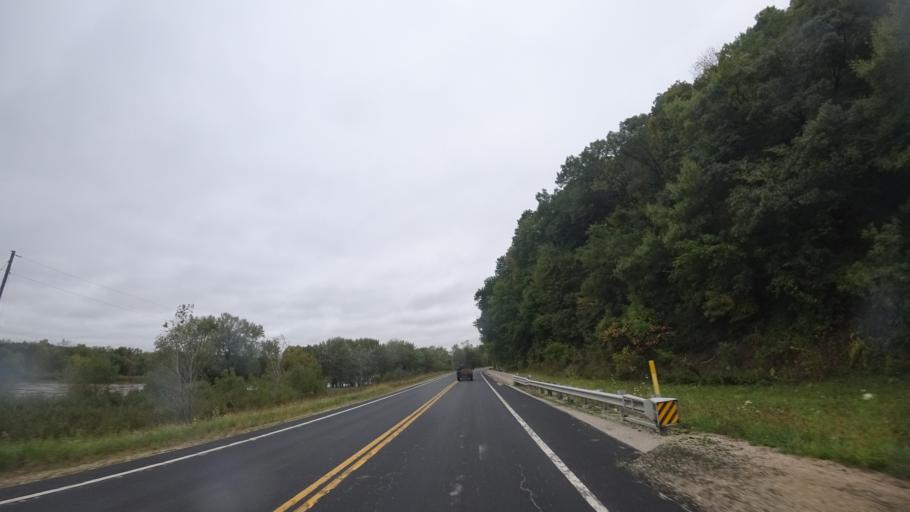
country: US
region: Wisconsin
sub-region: Grant County
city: Boscobel
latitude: 43.1365
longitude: -90.7436
